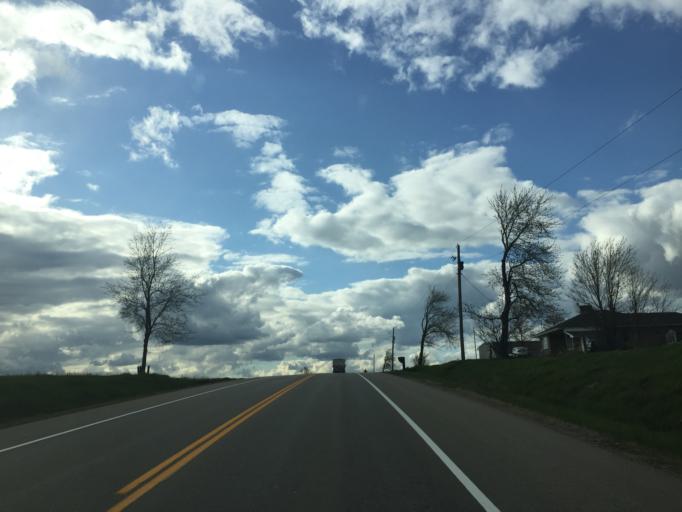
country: CA
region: Ontario
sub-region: Wellington County
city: Guelph
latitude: 43.5223
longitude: -80.3281
